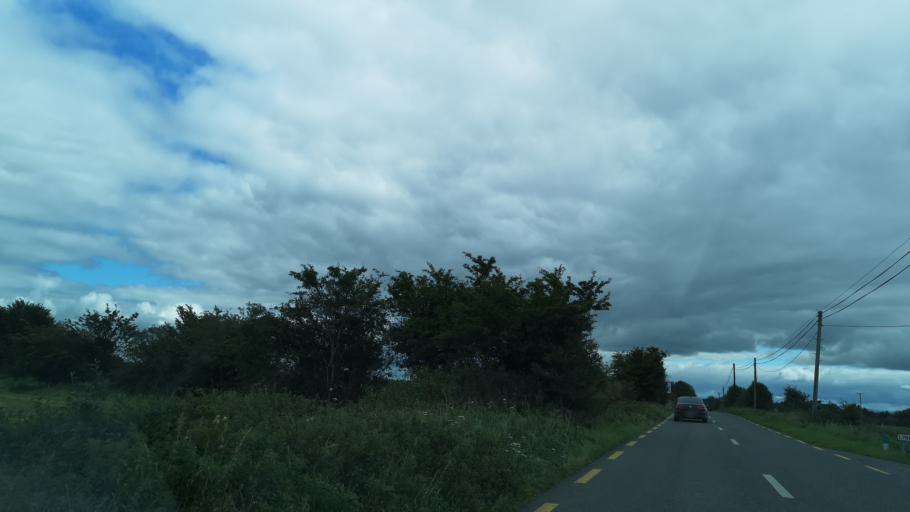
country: IE
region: Connaught
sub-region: County Galway
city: Ballinasloe
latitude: 53.2892
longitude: -8.0872
